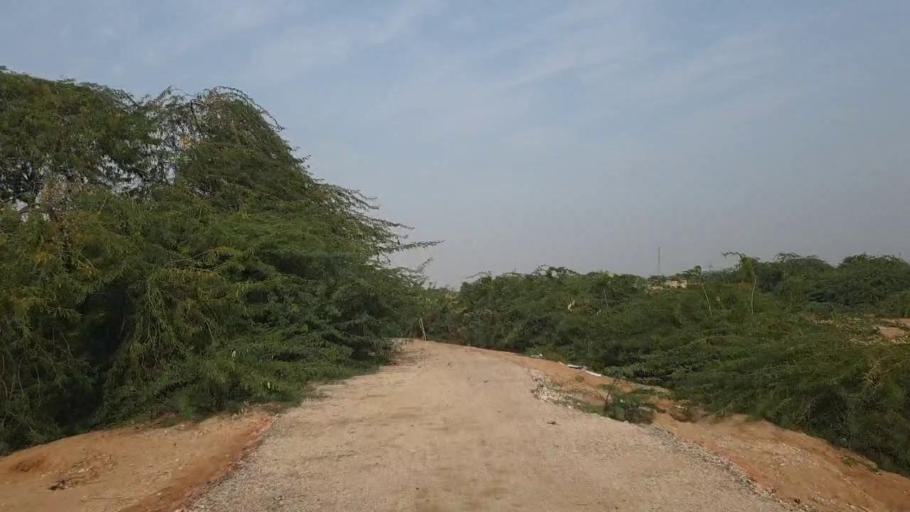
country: PK
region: Sindh
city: Sann
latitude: 26.0569
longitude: 68.1089
